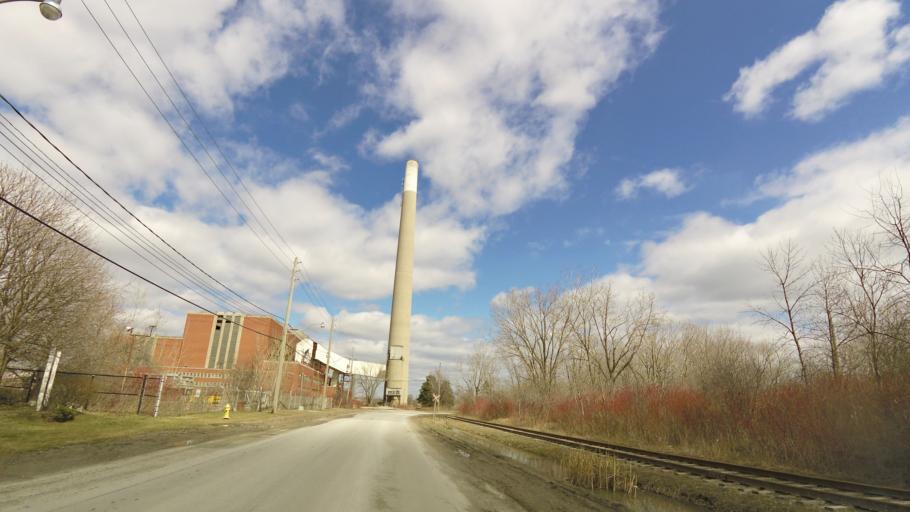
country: CA
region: Ontario
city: Toronto
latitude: 43.6442
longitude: -79.3372
